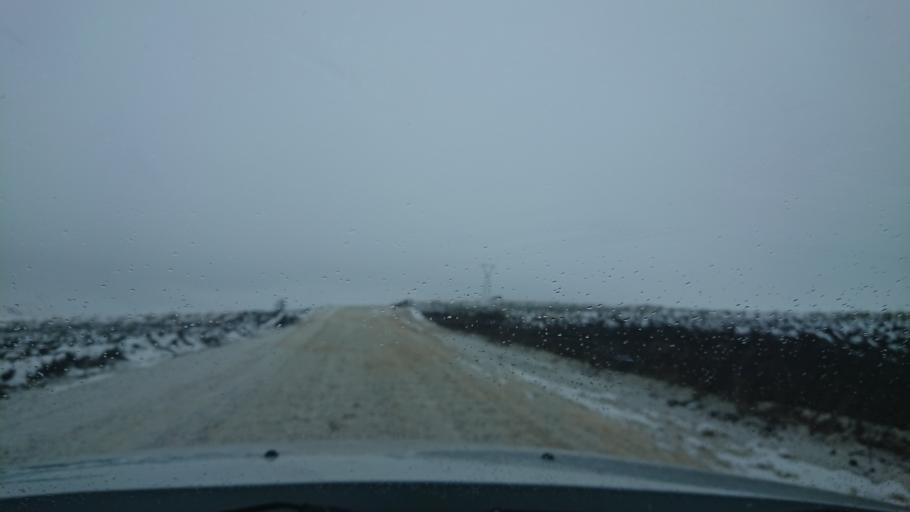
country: TR
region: Aksaray
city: Agacoren
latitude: 38.8480
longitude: 33.9464
